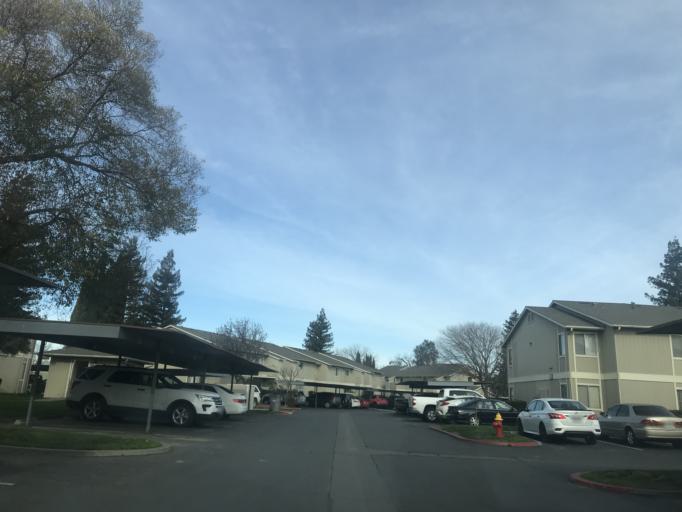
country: US
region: California
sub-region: Yolo County
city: Woodland
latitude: 38.6648
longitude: -121.7579
